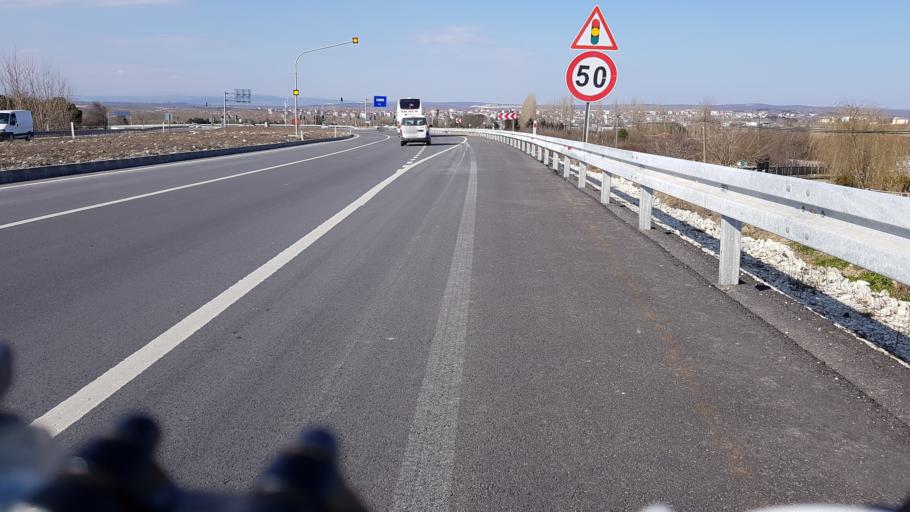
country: TR
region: Tekirdag
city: Saray
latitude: 41.4164
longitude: 27.9223
